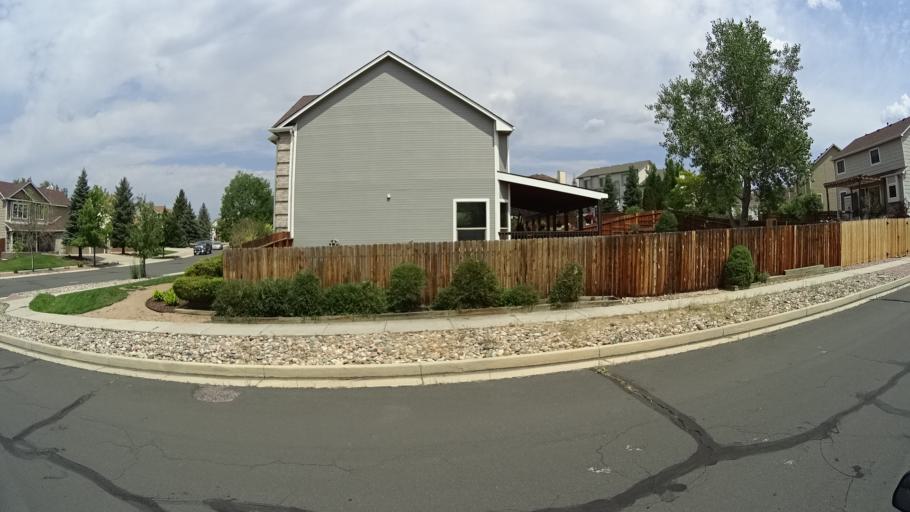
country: US
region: Colorado
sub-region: El Paso County
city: Black Forest
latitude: 38.9620
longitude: -104.7742
